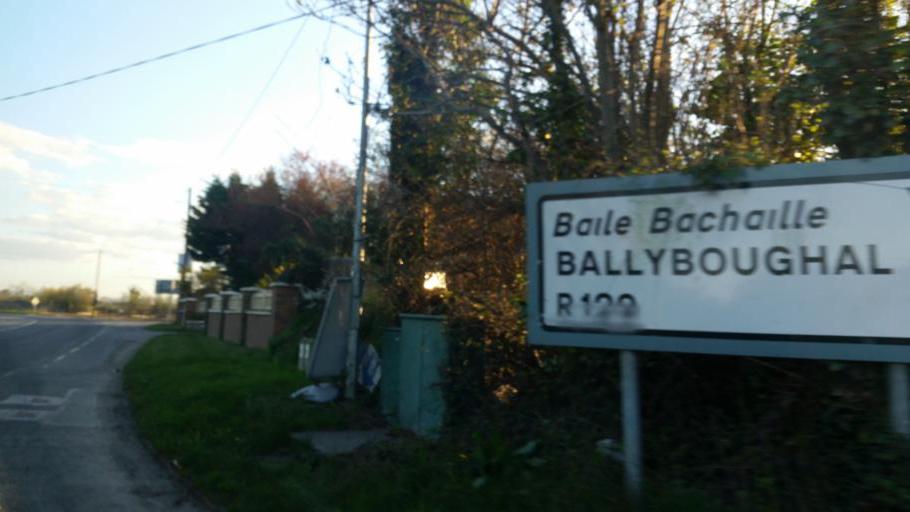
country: IE
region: Leinster
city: Lusk
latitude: 53.5063
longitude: -6.1940
